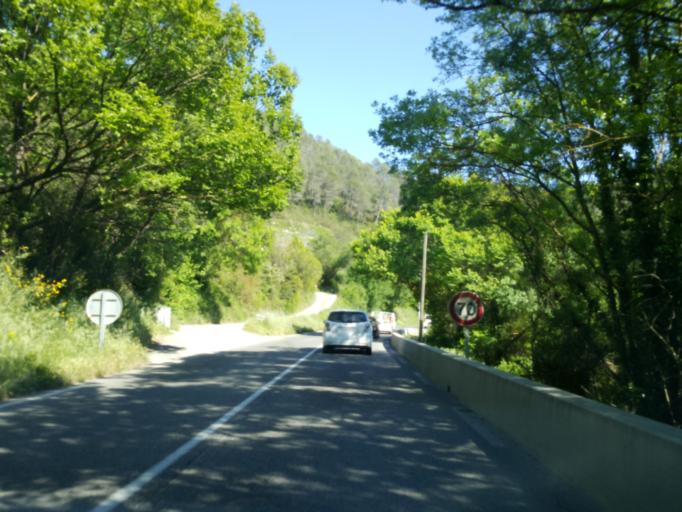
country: FR
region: Provence-Alpes-Cote d'Azur
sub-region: Departement du Var
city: Belgentier
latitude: 43.2372
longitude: 6.0066
